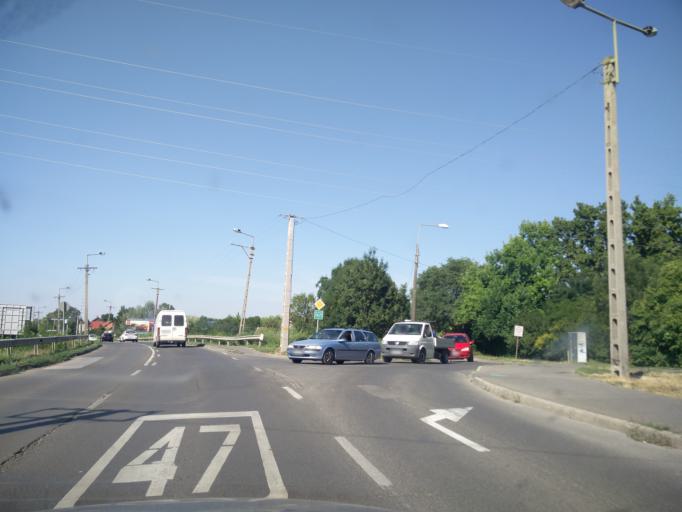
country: HU
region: Csongrad
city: Szeged
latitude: 46.2759
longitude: 20.1658
